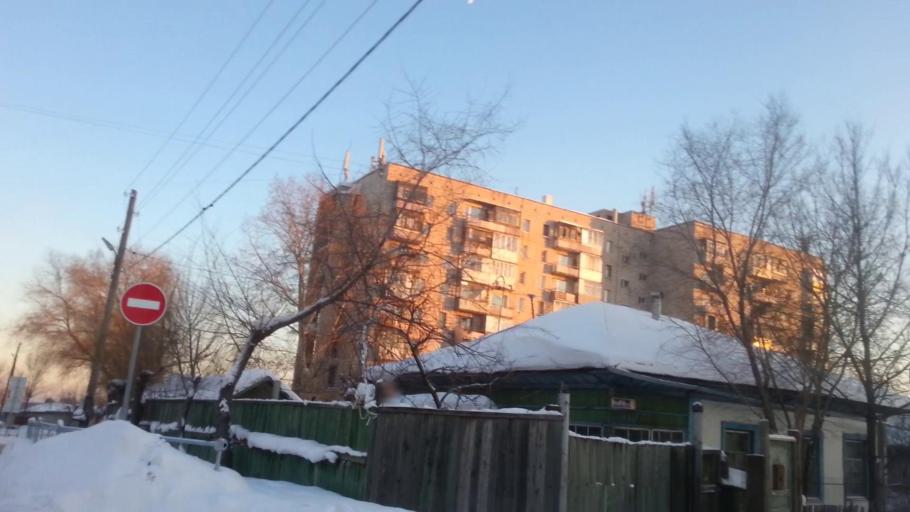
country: RU
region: Altai Krai
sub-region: Gorod Barnaulskiy
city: Barnaul
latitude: 53.3536
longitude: 83.7045
